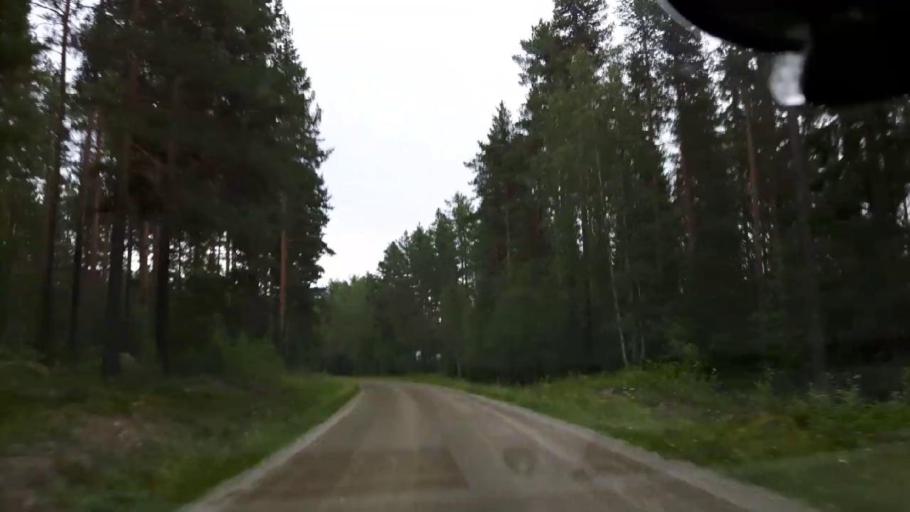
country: SE
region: Jaemtland
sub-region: Braecke Kommun
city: Braecke
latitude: 62.9328
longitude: 15.4743
